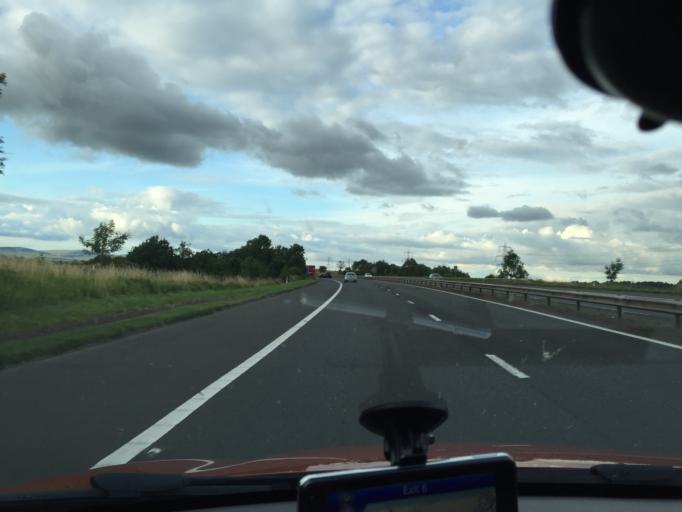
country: GB
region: Scotland
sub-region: North Lanarkshire
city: Glenboig
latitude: 55.8945
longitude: -4.0697
